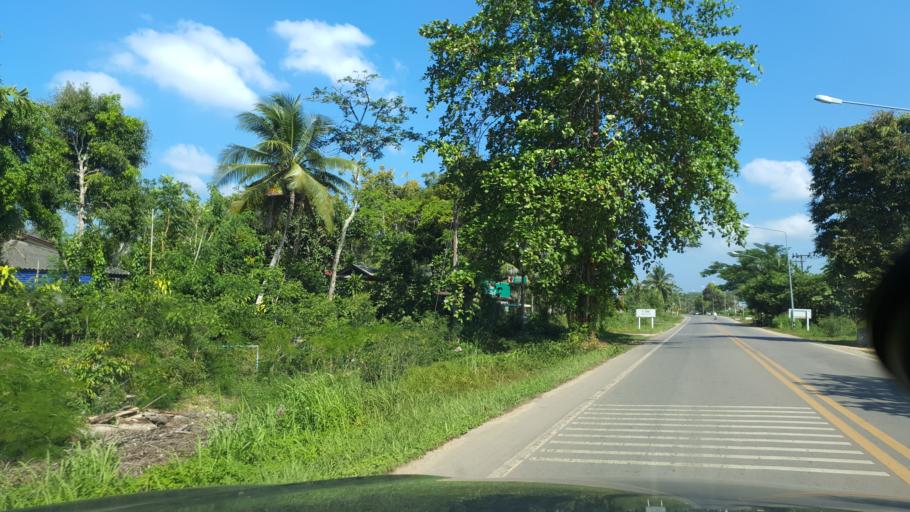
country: TH
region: Phangnga
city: Ban Ao Nang
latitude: 8.0573
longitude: 98.8587
